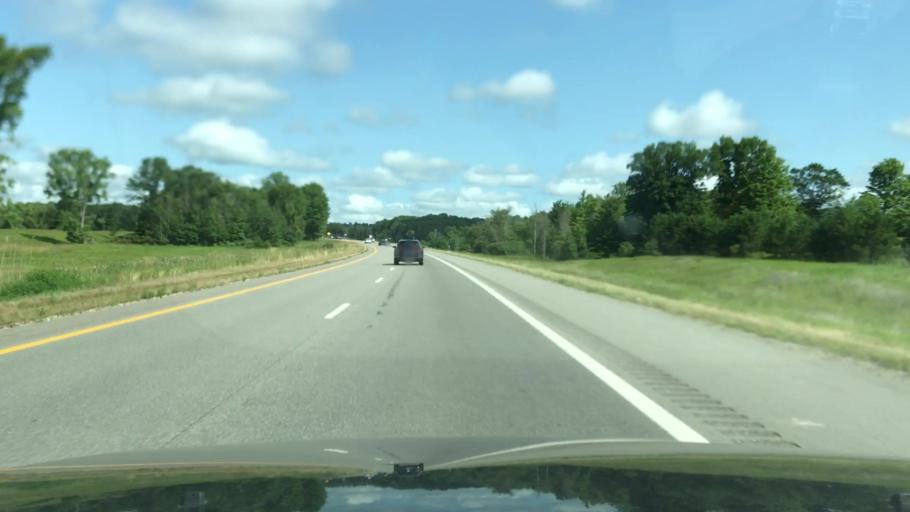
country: US
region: Michigan
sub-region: Mecosta County
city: Big Rapids
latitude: 43.6222
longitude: -85.4986
